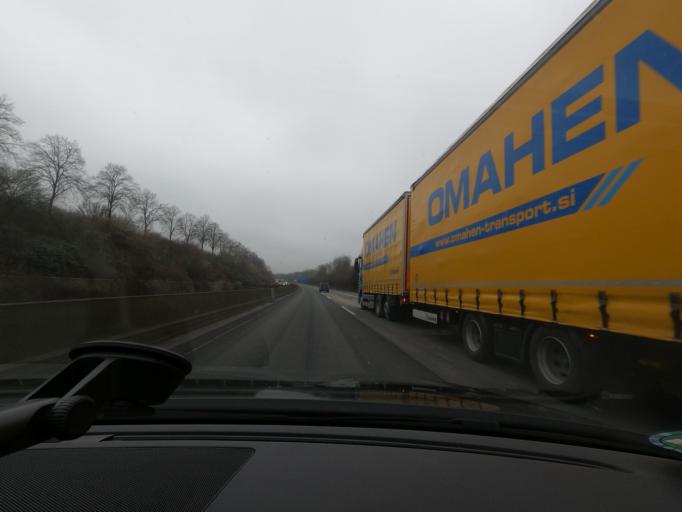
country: DE
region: North Rhine-Westphalia
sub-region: Regierungsbezirk Koln
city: Bergheim
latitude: 50.9309
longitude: 6.6650
